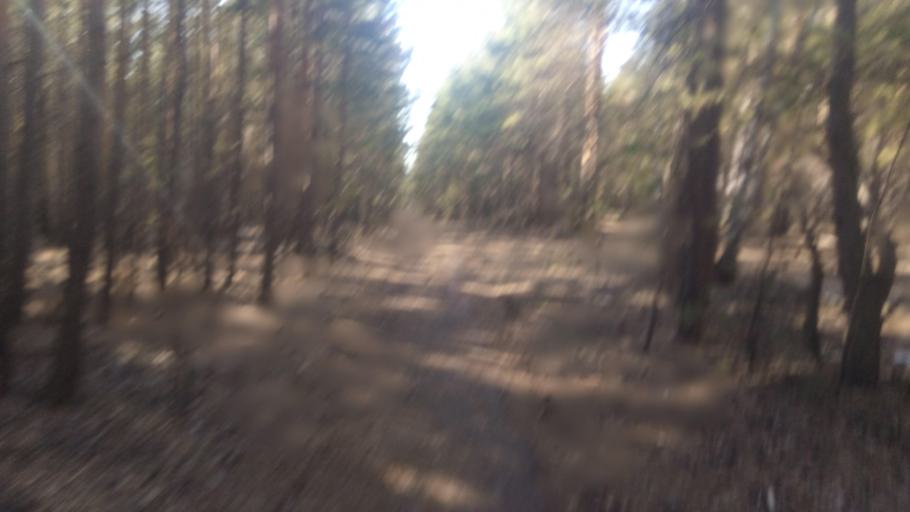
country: RU
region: Chelyabinsk
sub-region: Gorod Chelyabinsk
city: Chelyabinsk
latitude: 55.1588
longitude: 61.3403
